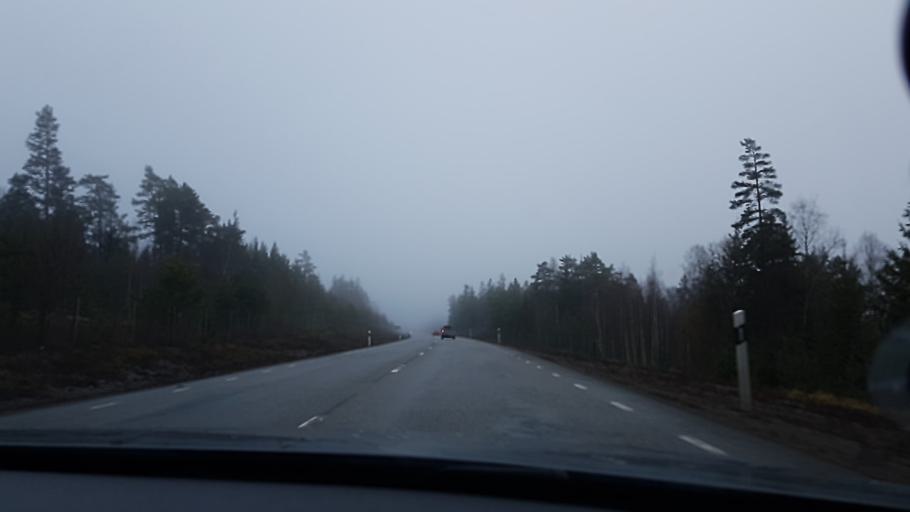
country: SE
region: Vaestra Goetaland
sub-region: Gullspangs Kommun
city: Gullspang
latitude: 58.8947
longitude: 14.0172
